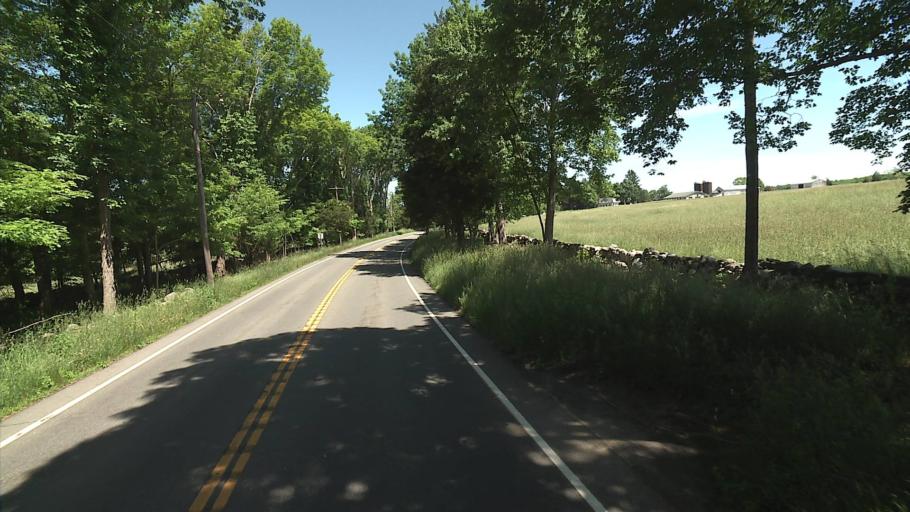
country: US
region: Rhode Island
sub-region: Washington County
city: Hopkinton
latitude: 41.5127
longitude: -71.8415
